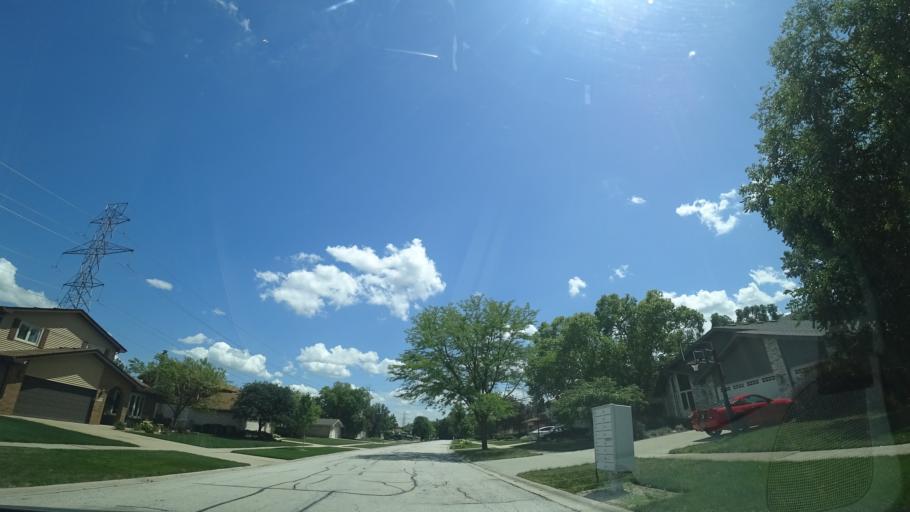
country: US
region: Illinois
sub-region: Will County
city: Homer Glen
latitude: 41.5735
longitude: -87.8981
